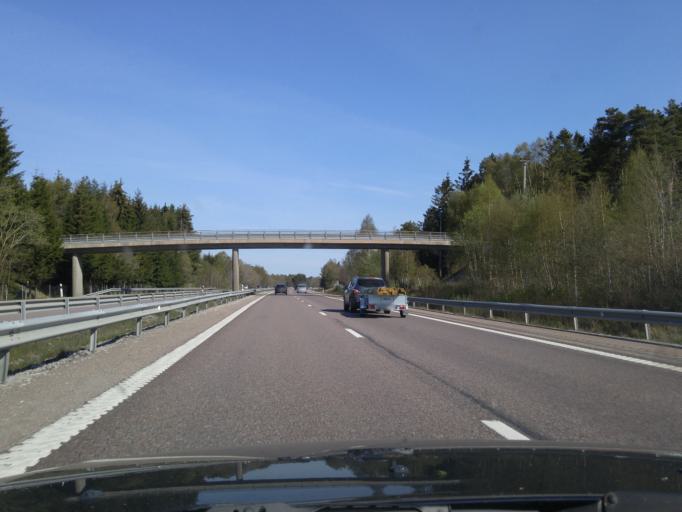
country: SE
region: Vaestra Goetaland
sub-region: Kungalvs Kommun
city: Kode
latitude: 57.9610
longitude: 11.8456
